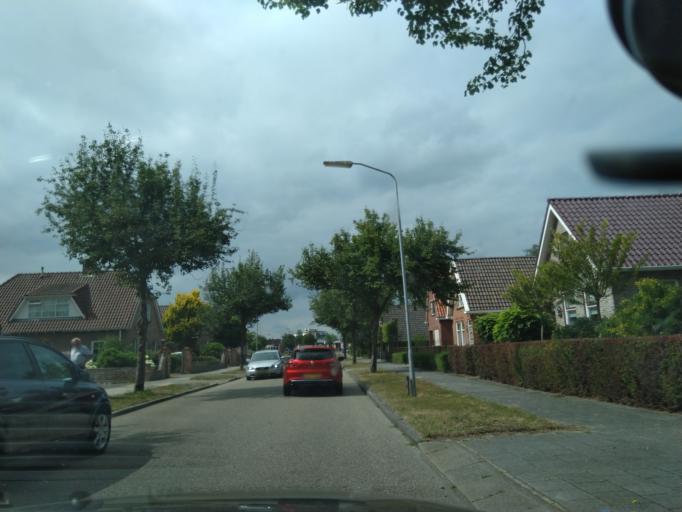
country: NL
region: Groningen
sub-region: Gemeente Pekela
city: Oude Pekela
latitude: 53.0788
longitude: 6.9725
